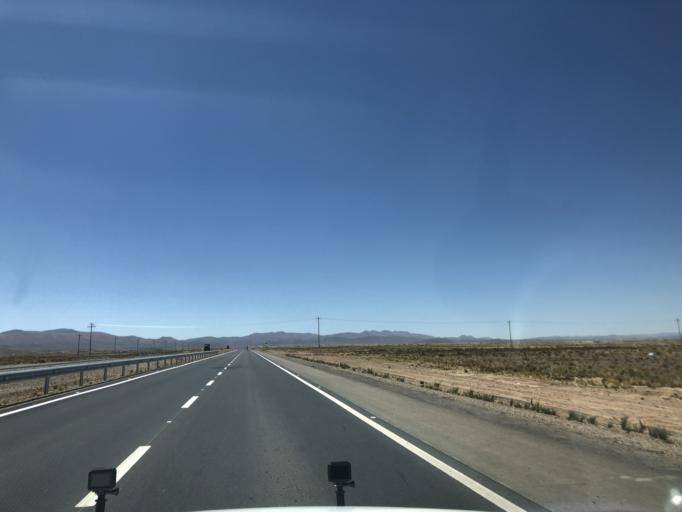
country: BO
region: La Paz
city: Colquiri
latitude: -17.6506
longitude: -67.1836
